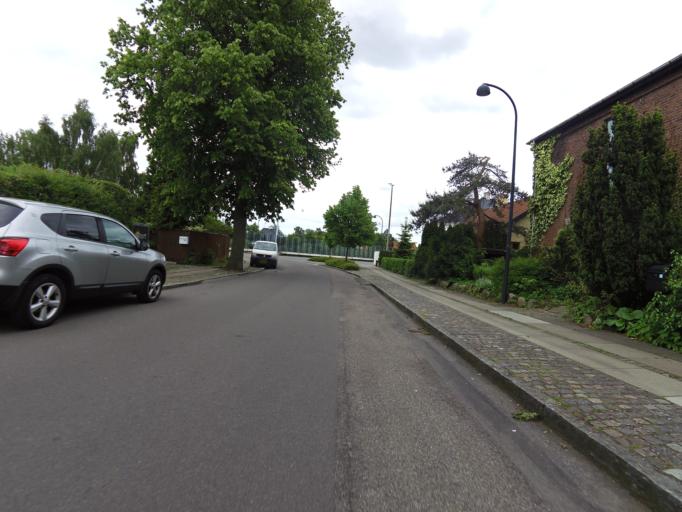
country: DK
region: Capital Region
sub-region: Gentofte Kommune
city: Charlottenlund
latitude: 55.7291
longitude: 12.5475
